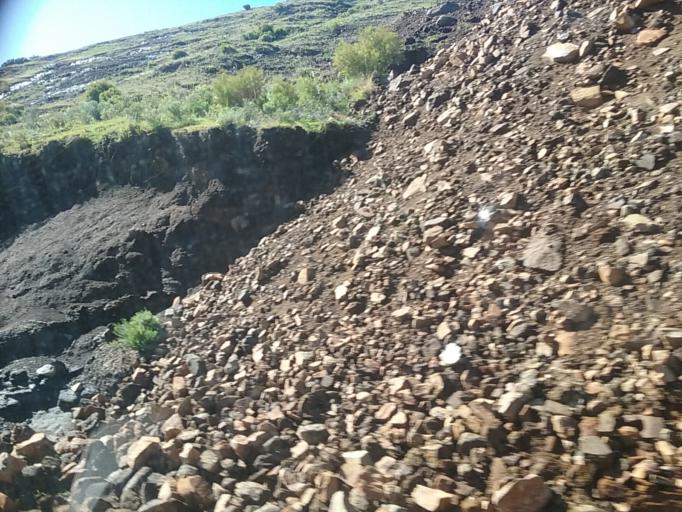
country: LS
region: Berea
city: Teyateyaneng
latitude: -29.2346
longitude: 27.9192
